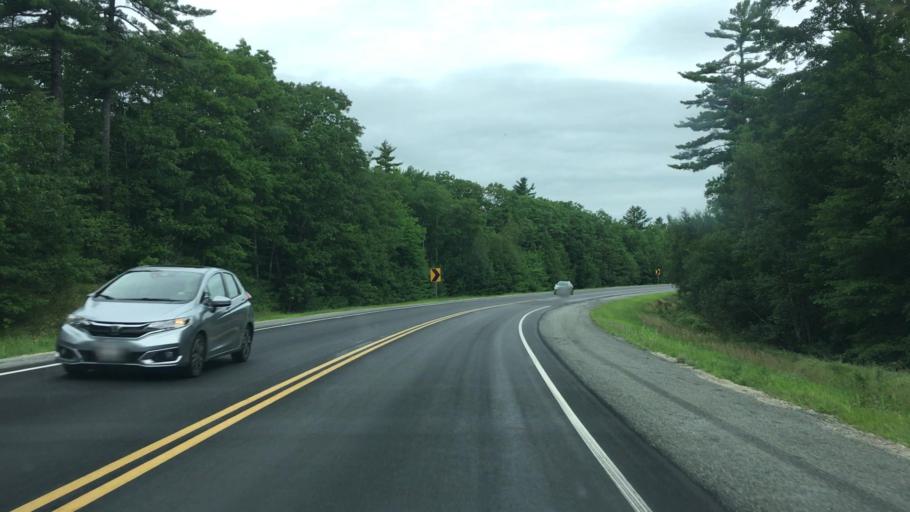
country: US
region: Maine
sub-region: Washington County
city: Cherryfield
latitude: 44.9068
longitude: -67.8570
